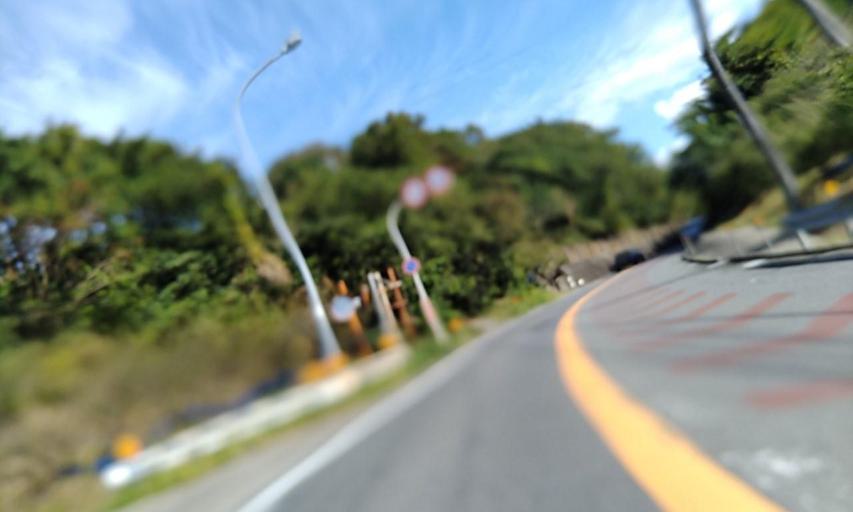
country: JP
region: Wakayama
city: Tanabe
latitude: 33.7803
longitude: 135.2982
